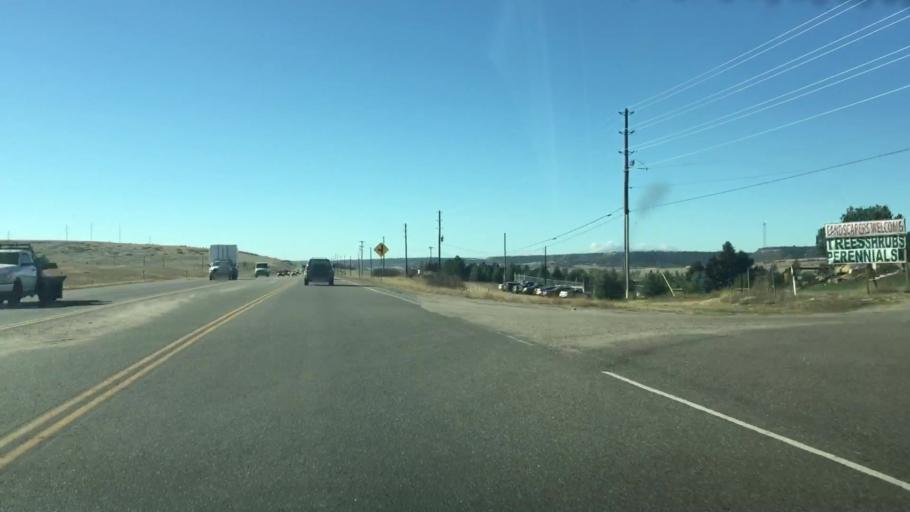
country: US
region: Colorado
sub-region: Douglas County
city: The Pinery
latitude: 39.4302
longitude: -104.7605
